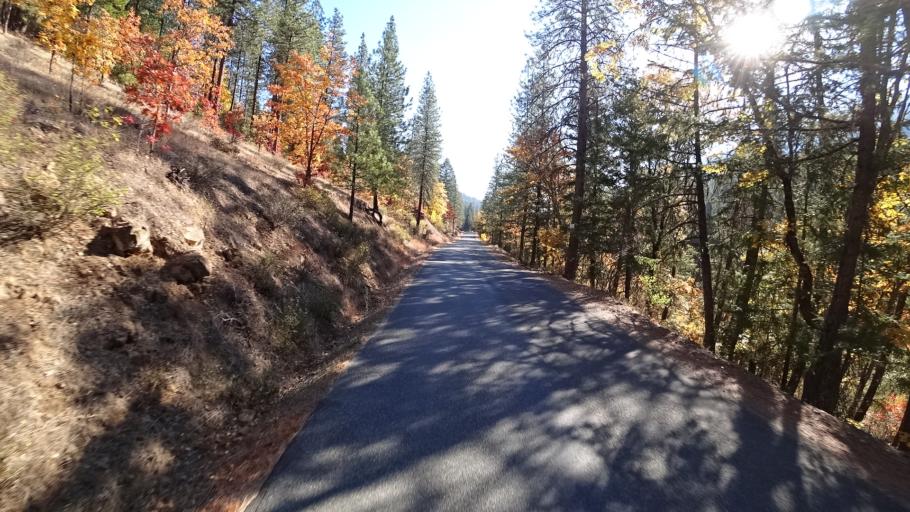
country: US
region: California
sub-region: Siskiyou County
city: Happy Camp
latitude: 41.6454
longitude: -123.0411
